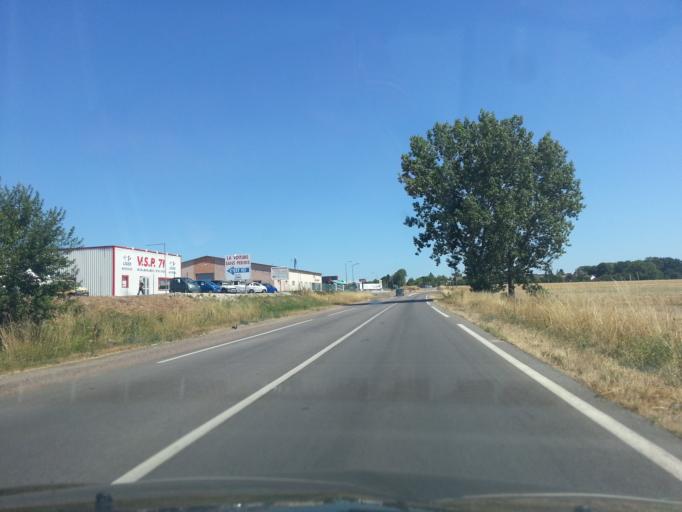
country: FR
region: Bourgogne
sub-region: Departement de Saone-et-Loire
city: Chatenoy-le-Royal
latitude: 46.7809
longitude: 4.7952
